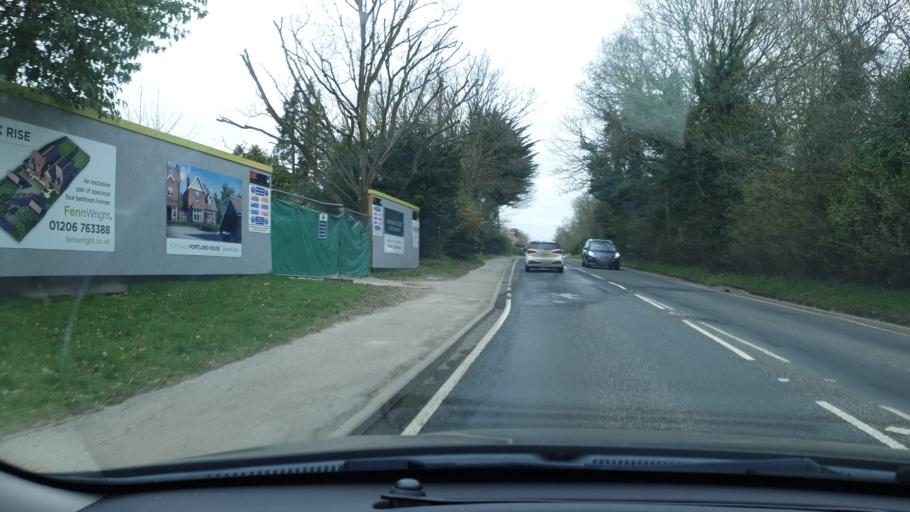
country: GB
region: England
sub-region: Essex
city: Great Horkesley
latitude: 51.9247
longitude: 0.8823
